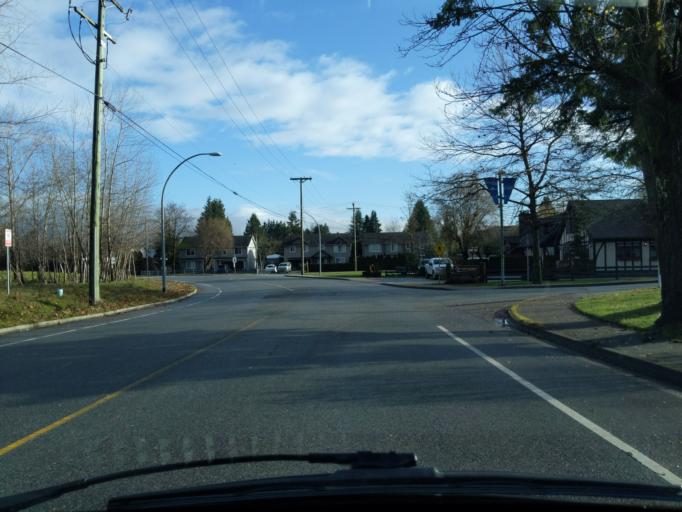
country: CA
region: British Columbia
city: Pitt Meadows
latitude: 49.2179
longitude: -122.6662
